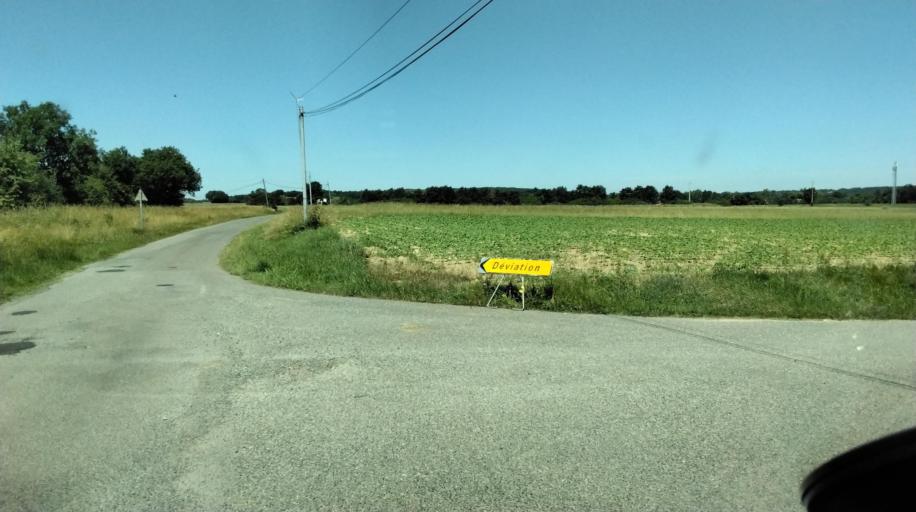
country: FR
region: Midi-Pyrenees
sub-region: Departement de la Haute-Garonne
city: Sainte-Foy-de-Peyrolieres
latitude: 43.4838
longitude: 1.1405
